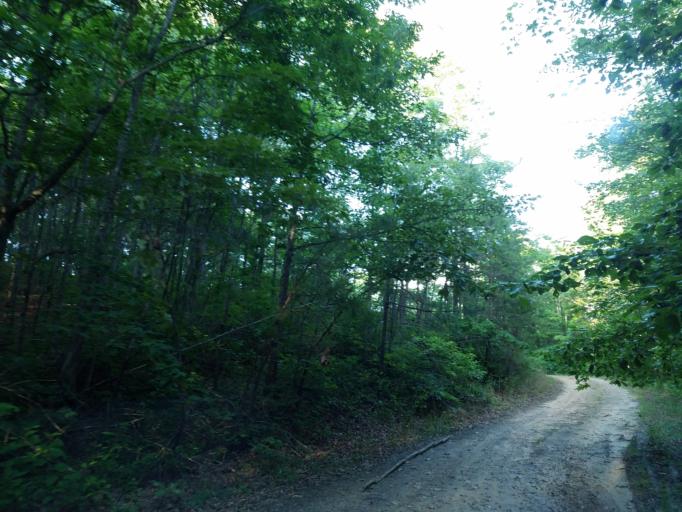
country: US
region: Georgia
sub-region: Fannin County
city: Blue Ridge
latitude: 34.8115
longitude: -84.1591
